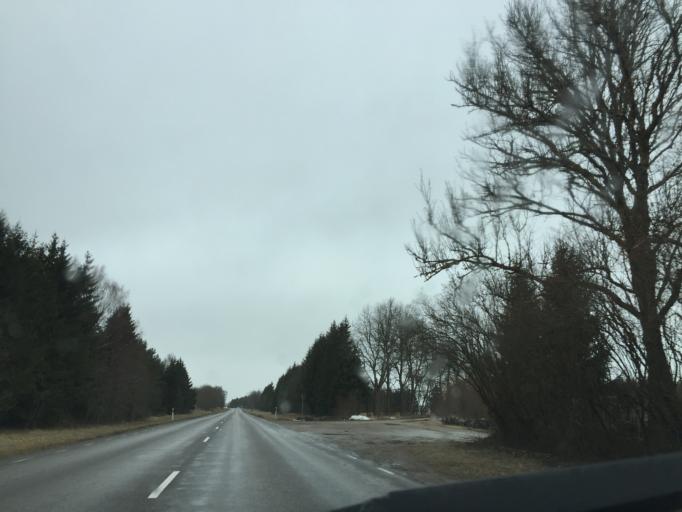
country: EE
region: Laeaene
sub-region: Ridala Parish
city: Uuemoisa
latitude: 58.8747
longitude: 23.6127
